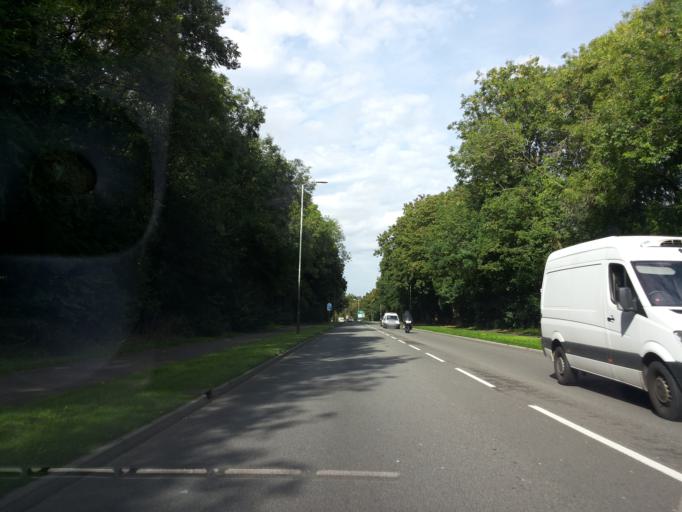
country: GB
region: England
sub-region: Greater London
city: Orpington
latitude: 51.3536
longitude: 0.0876
